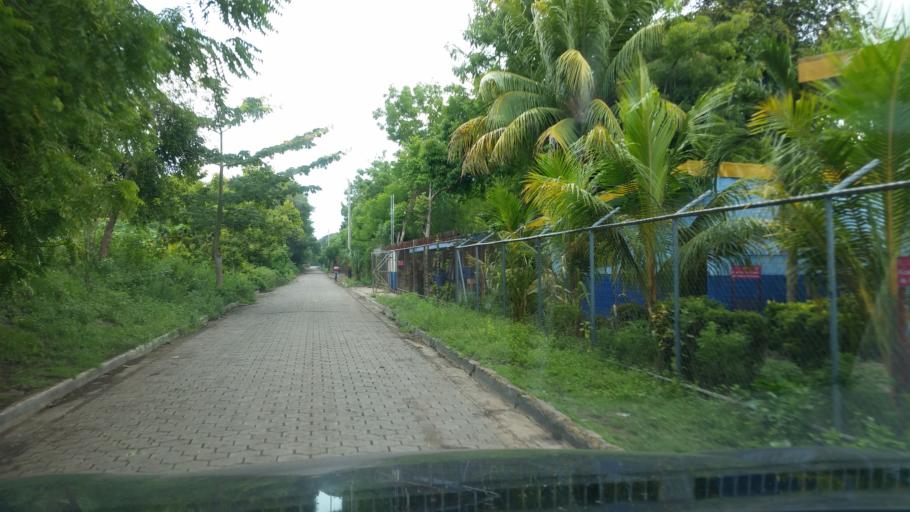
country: NI
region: Chinandega
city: Puerto Morazan
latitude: 12.7723
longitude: -87.1338
